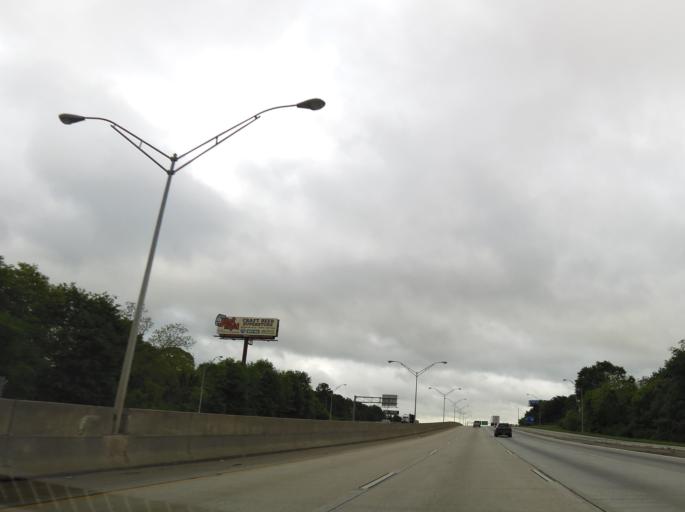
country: US
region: Georgia
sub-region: Monroe County
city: Forsyth
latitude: 33.0417
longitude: -83.9358
